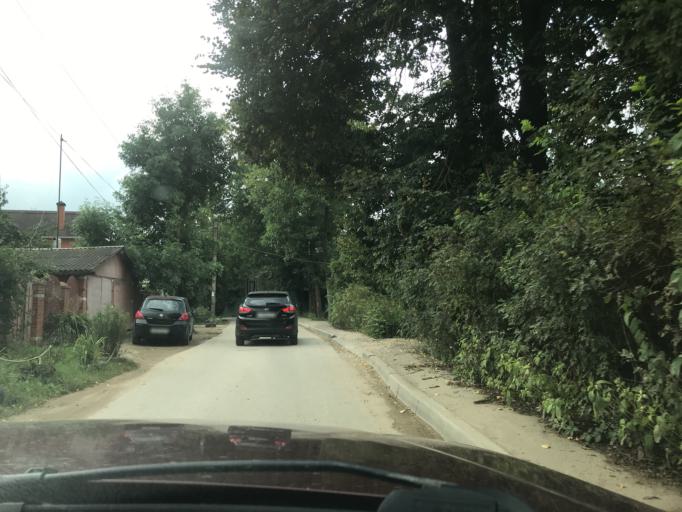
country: RU
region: Kaluga
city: Kaluga
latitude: 54.5357
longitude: 36.2406
